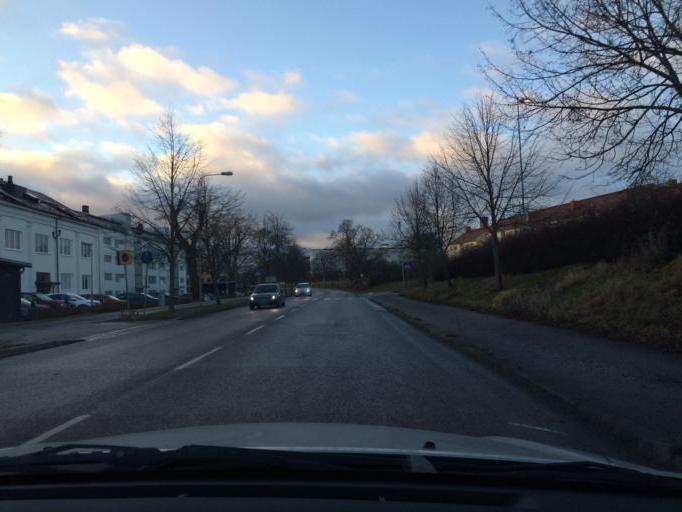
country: SE
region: Soedermanland
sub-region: Eskilstuna Kommun
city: Eskilstuna
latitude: 59.3661
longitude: 16.5128
